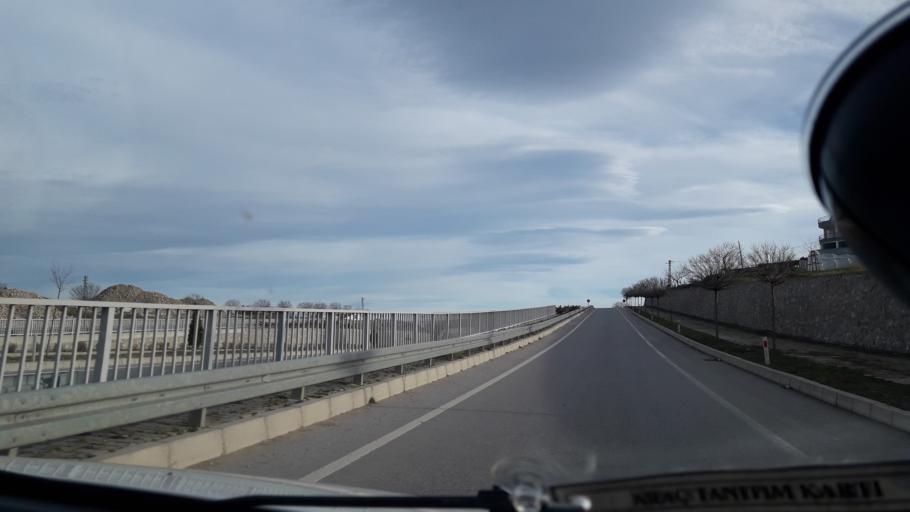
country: TR
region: Sinop
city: Gerze
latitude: 41.8031
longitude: 35.1763
